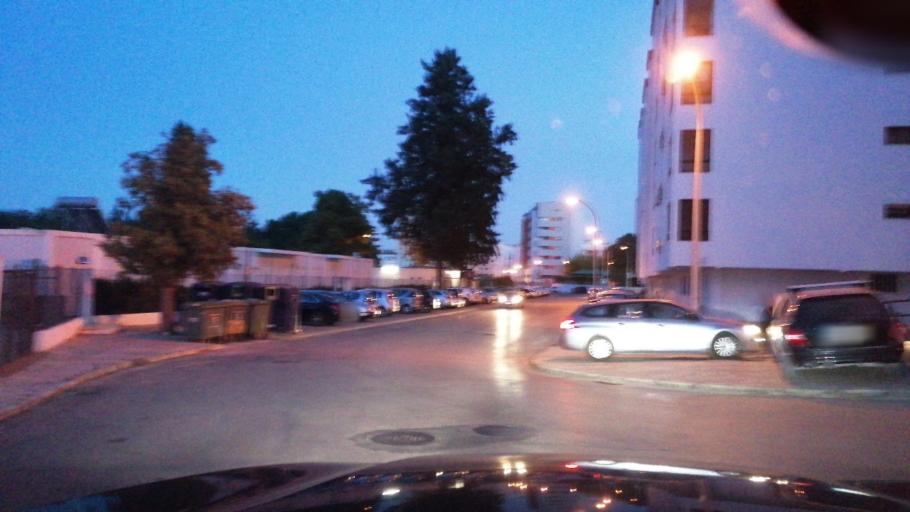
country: PT
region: Setubal
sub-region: Setubal
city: Setubal
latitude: 38.5425
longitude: -8.8940
